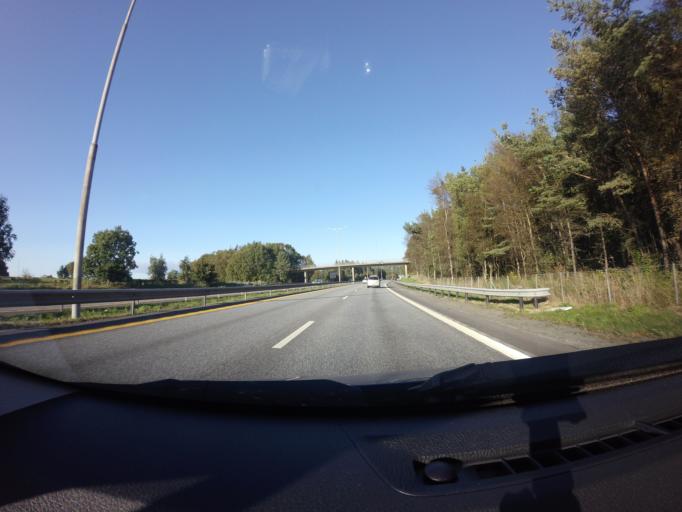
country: NO
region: Rogaland
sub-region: Sola
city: Sola
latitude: 58.9167
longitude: 5.6978
